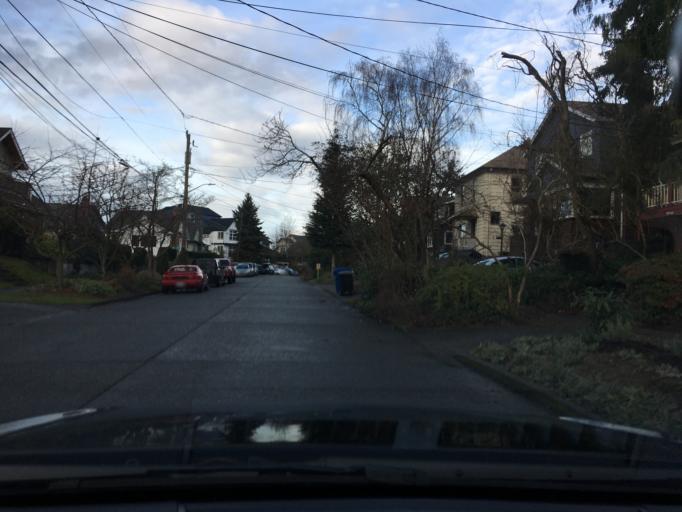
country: US
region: Washington
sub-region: King County
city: Seattle
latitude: 47.6697
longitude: -122.3379
